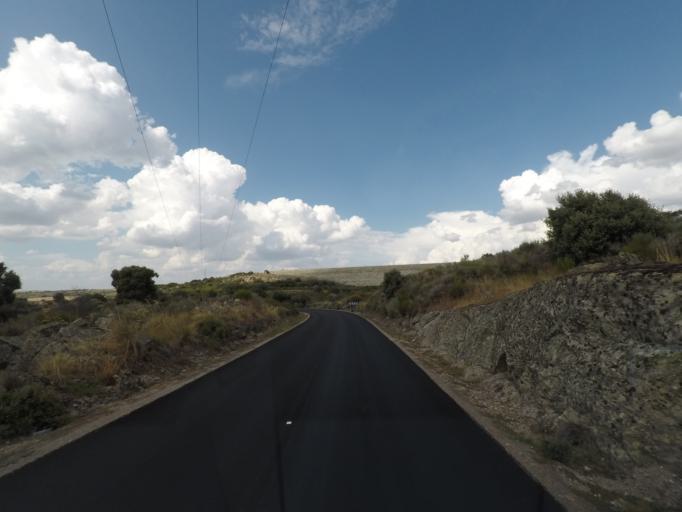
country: ES
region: Castille and Leon
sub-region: Provincia de Salamanca
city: Almendra
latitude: 41.2800
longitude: -6.3314
